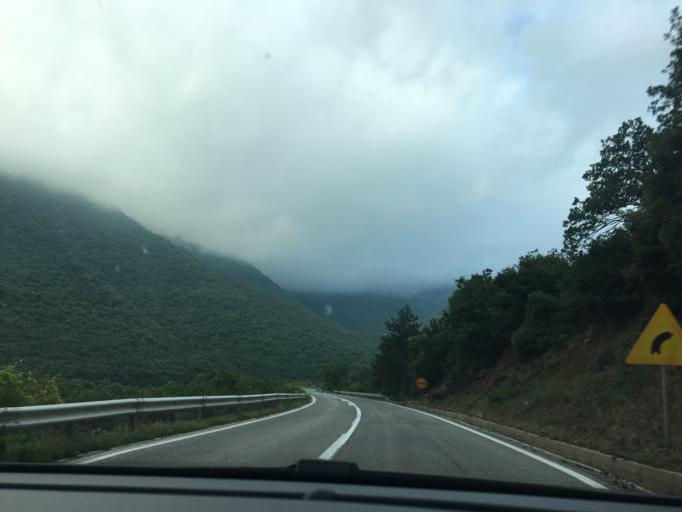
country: MK
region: Gevgelija
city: Miravci
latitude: 41.3886
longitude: 22.3682
